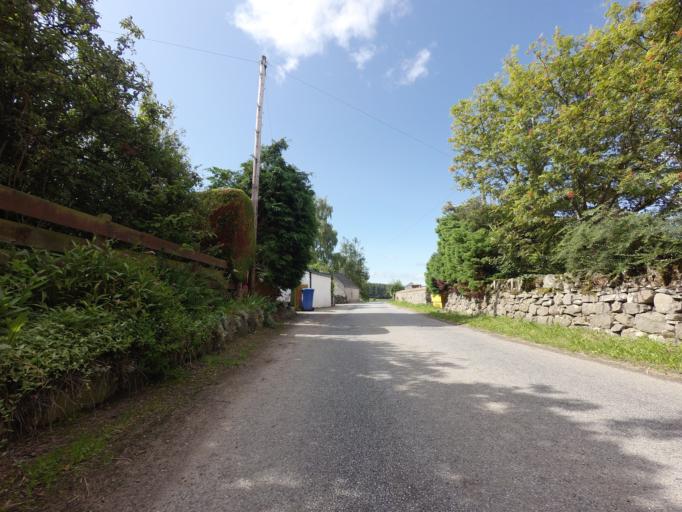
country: GB
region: Scotland
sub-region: Highland
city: Nairn
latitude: 57.5388
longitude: -3.8667
